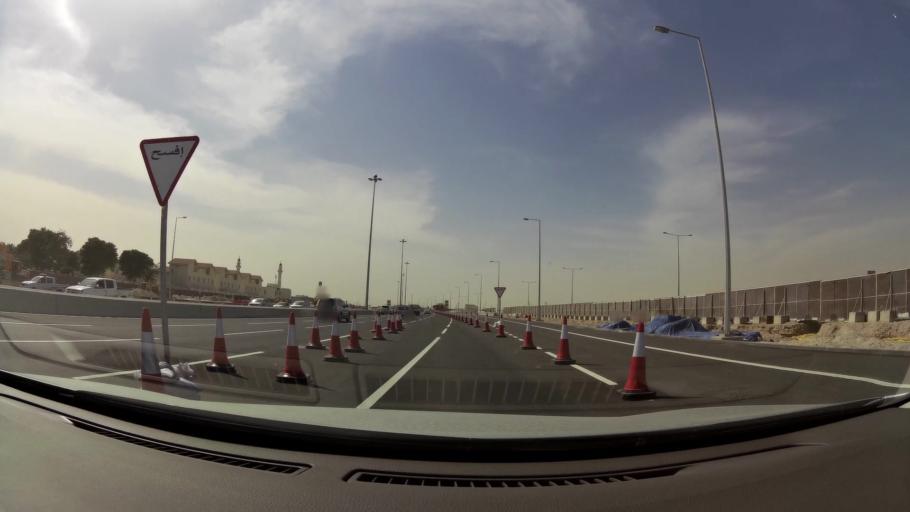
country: QA
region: Baladiyat ar Rayyan
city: Ar Rayyan
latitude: 25.3044
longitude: 51.4179
